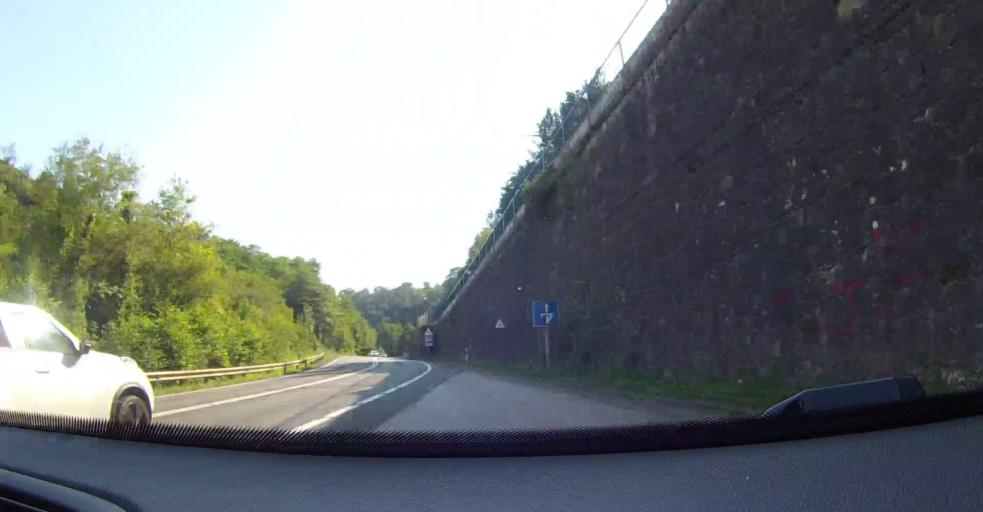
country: ES
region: Basque Country
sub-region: Bizkaia
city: Muxika
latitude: 43.2593
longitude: -2.6900
